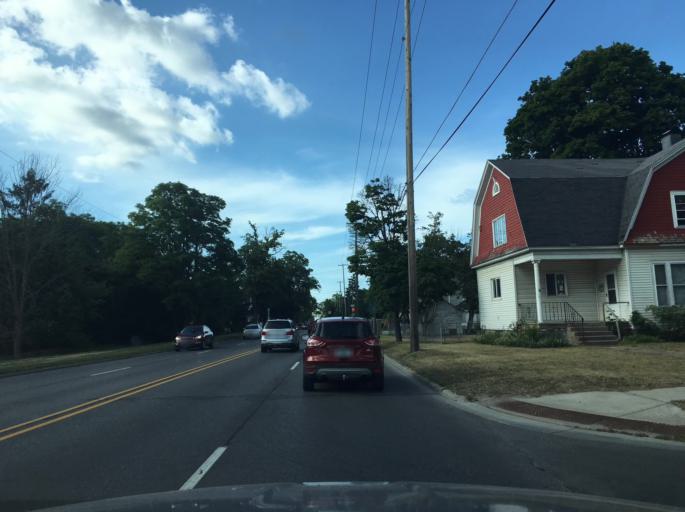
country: US
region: Michigan
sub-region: Grand Traverse County
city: Traverse City
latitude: 44.7581
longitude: -85.6347
